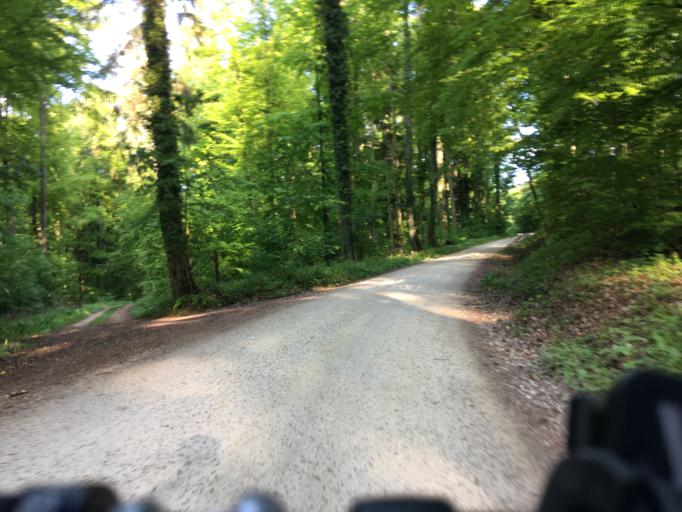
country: DE
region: Baden-Wuerttemberg
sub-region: Freiburg Region
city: Gailingen
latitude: 47.7088
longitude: 8.7472
